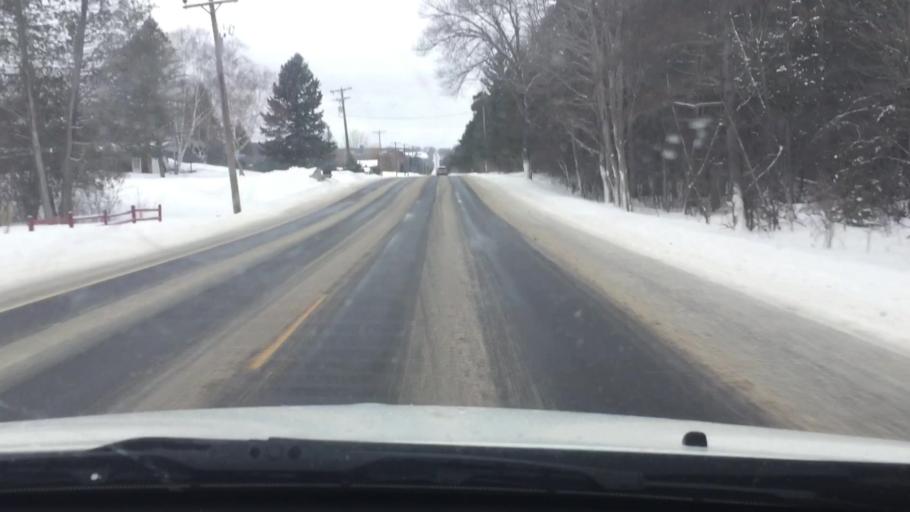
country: US
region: Michigan
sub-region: Charlevoix County
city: East Jordan
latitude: 45.1326
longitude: -85.1253
